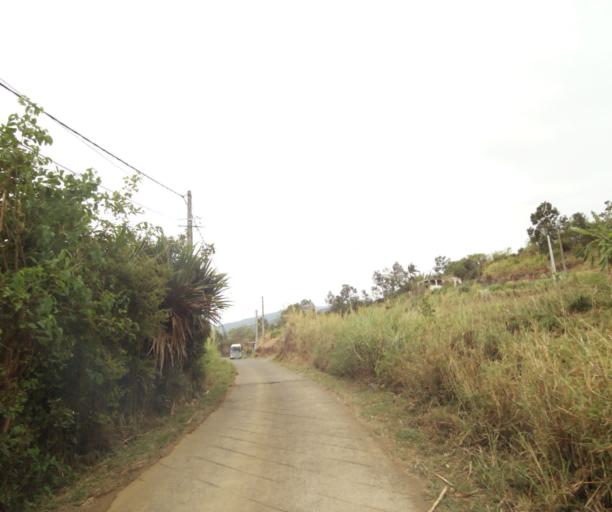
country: RE
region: Reunion
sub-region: Reunion
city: Saint-Paul
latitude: -21.0141
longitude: 55.3354
